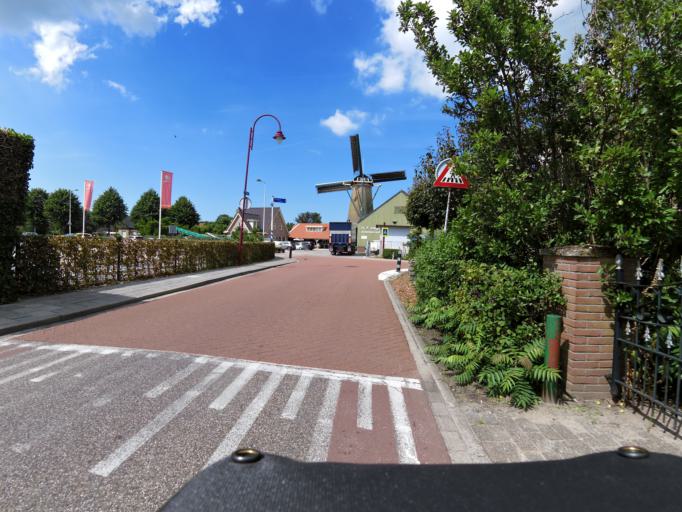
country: NL
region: South Holland
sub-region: Gemeente Goeree-Overflakkee
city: Ouddorp
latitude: 51.8119
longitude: 3.9336
